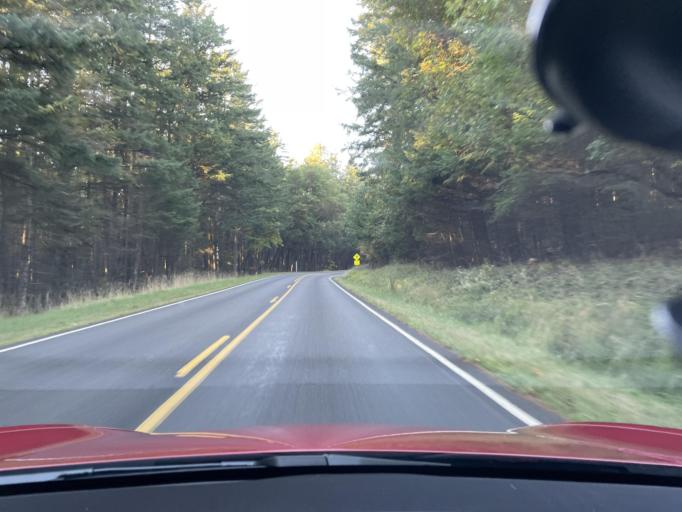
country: US
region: Washington
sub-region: San Juan County
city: Friday Harbor
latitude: 48.5827
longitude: -123.1444
